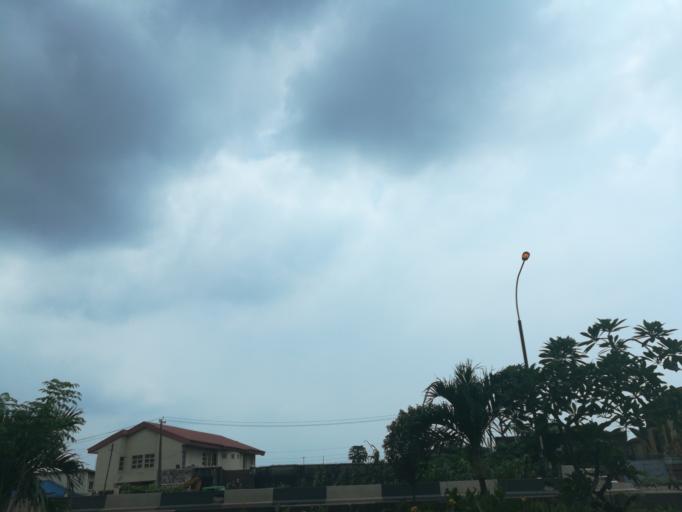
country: NG
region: Lagos
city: Ojota
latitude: 6.5755
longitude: 3.3971
